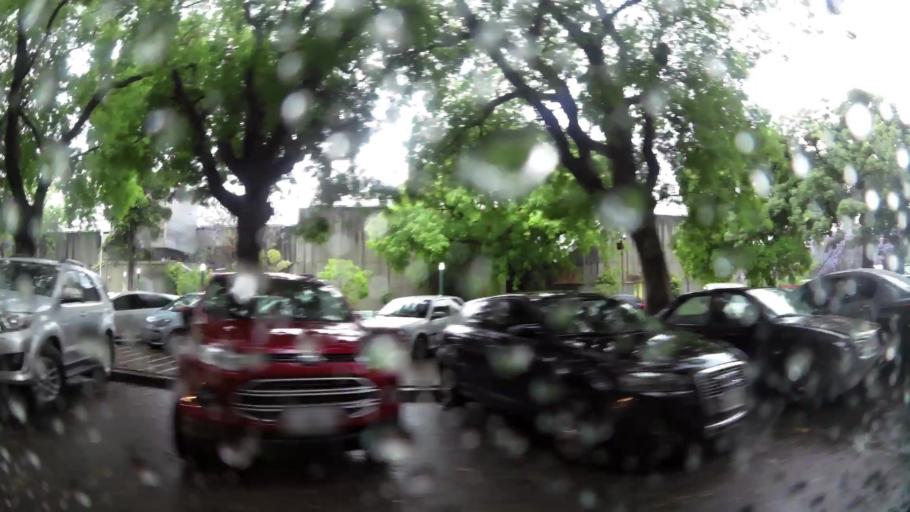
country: AR
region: Buenos Aires F.D.
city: Retiro
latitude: -34.5802
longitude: -58.3978
